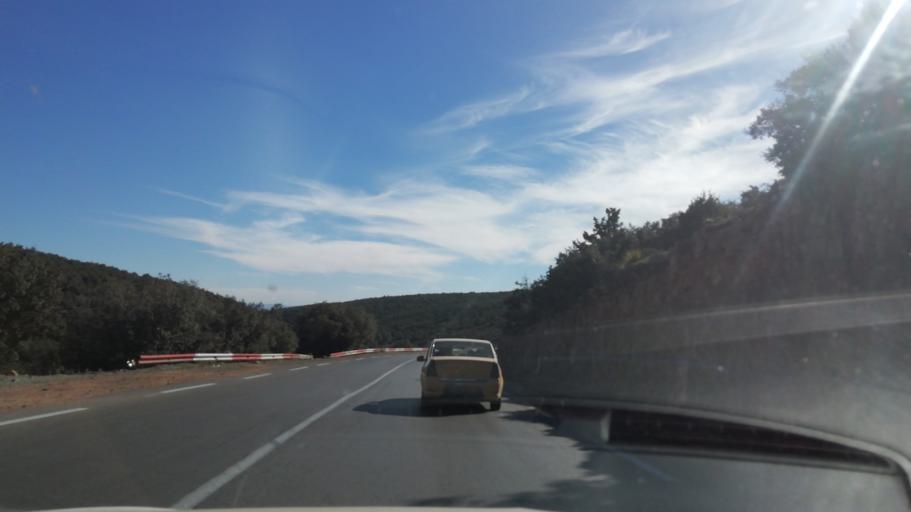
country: DZ
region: Tlemcen
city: Sebdou
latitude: 34.7468
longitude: -1.3499
